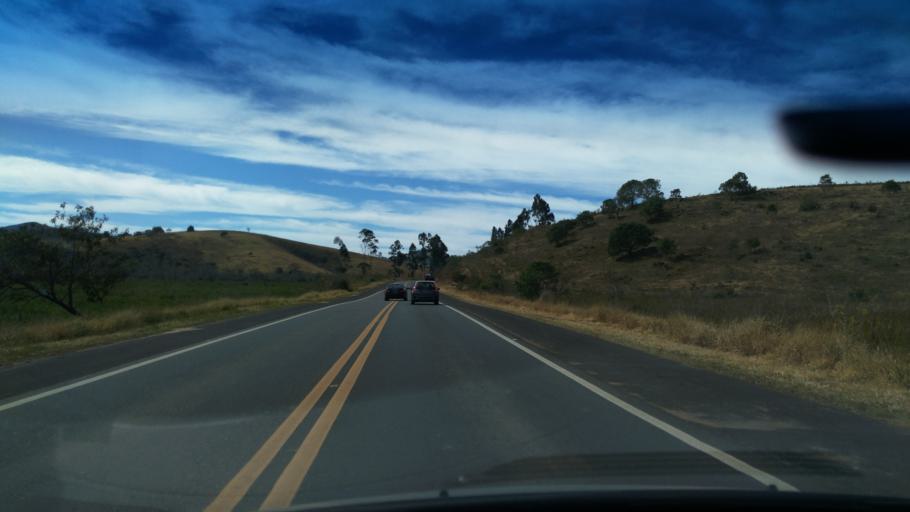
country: BR
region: Minas Gerais
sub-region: Borda Da Mata
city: Borda da Mata
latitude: -22.0742
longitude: -46.2624
